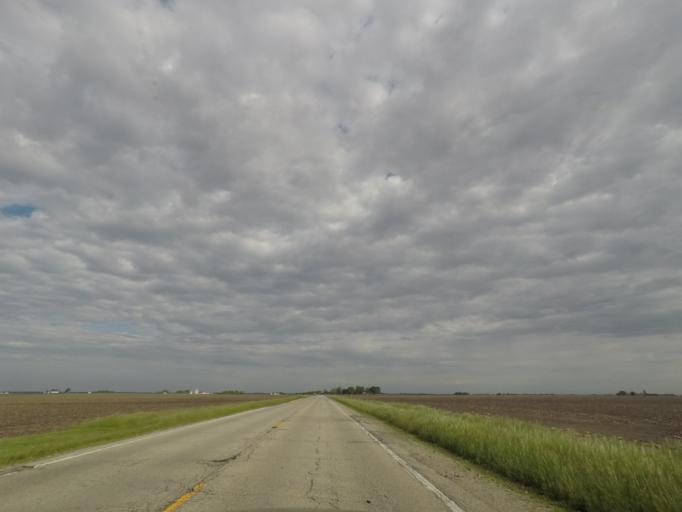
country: US
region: Illinois
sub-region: Logan County
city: Mount Pulaski
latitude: 40.0785
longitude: -89.2988
